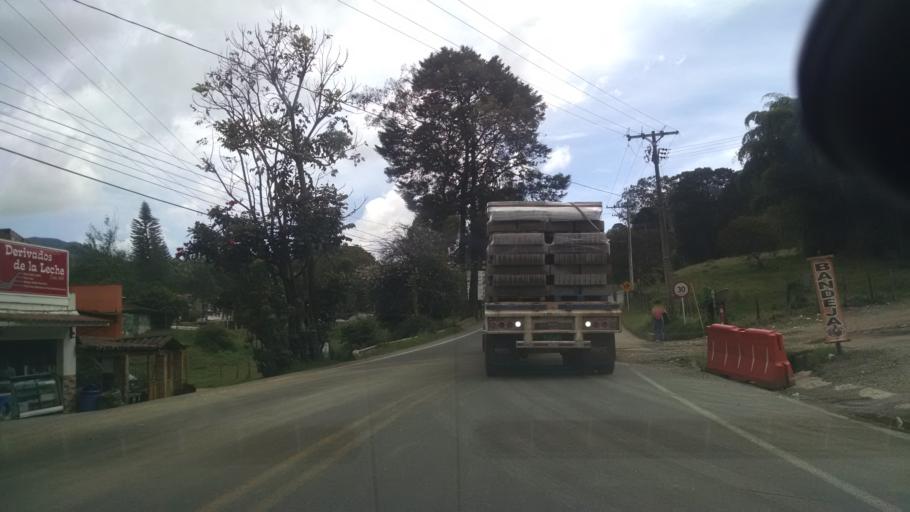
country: CO
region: Antioquia
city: Caldas
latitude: 6.0548
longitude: -75.6292
